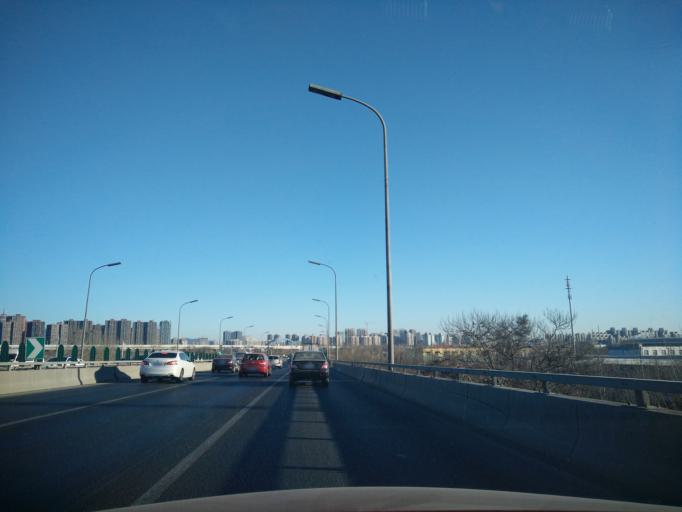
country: CN
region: Beijing
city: Lugu
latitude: 39.8817
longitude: 116.2026
